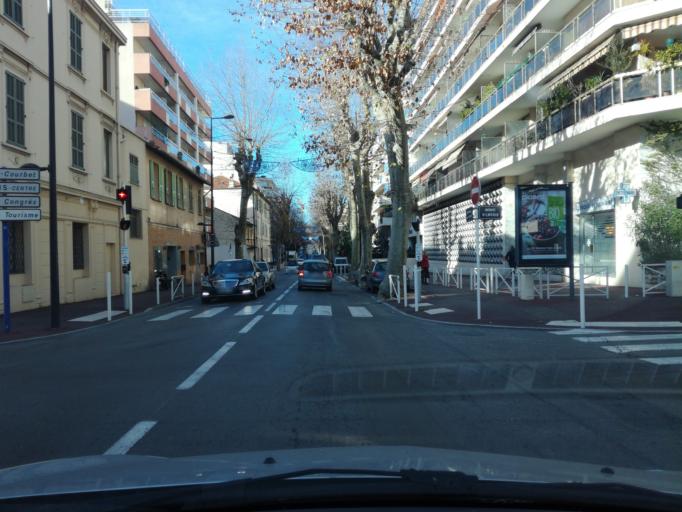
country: FR
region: Provence-Alpes-Cote d'Azur
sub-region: Departement des Alpes-Maritimes
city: Antibes
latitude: 43.5717
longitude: 7.1090
